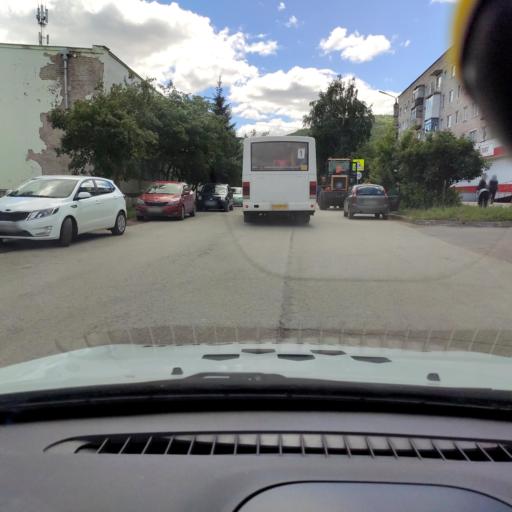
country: RU
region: Samara
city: Zhigulevsk
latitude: 53.4074
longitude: 49.4067
